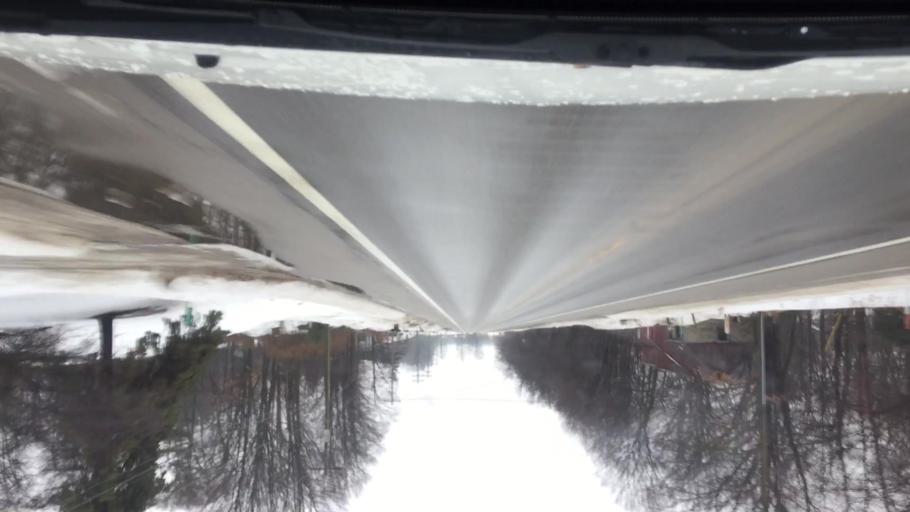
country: US
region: Michigan
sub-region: Charlevoix County
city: Charlevoix
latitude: 45.2875
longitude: -85.2445
